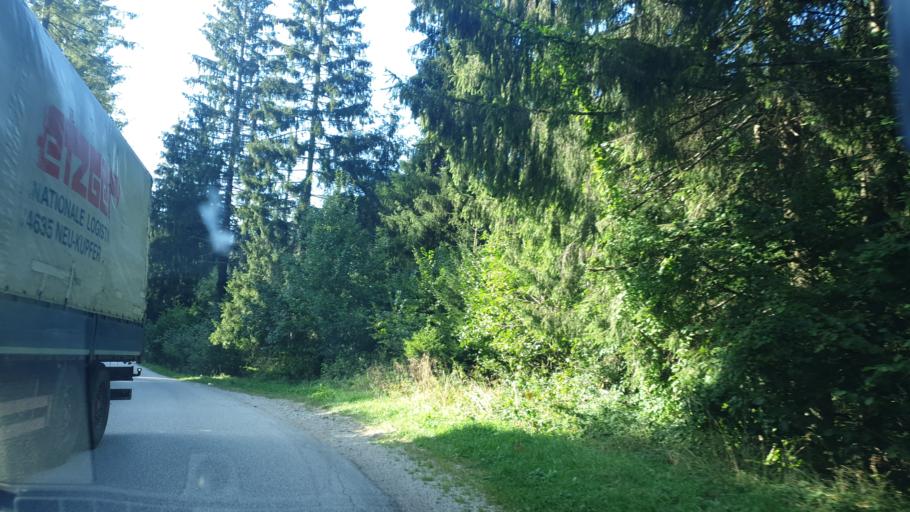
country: RS
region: Central Serbia
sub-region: Zlatiborski Okrug
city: Nova Varos
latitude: 43.4556
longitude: 19.8415
